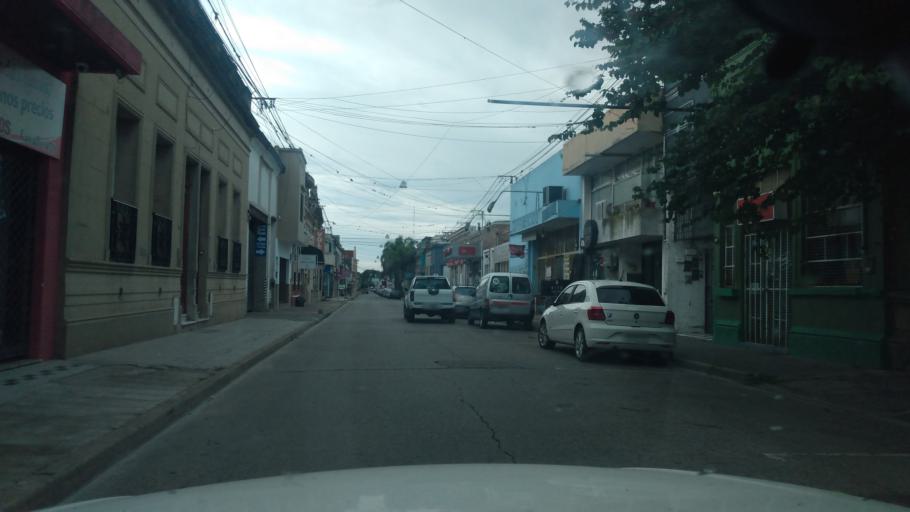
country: AR
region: Buenos Aires
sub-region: Partido de Lujan
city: Lujan
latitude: -34.5643
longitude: -59.1153
